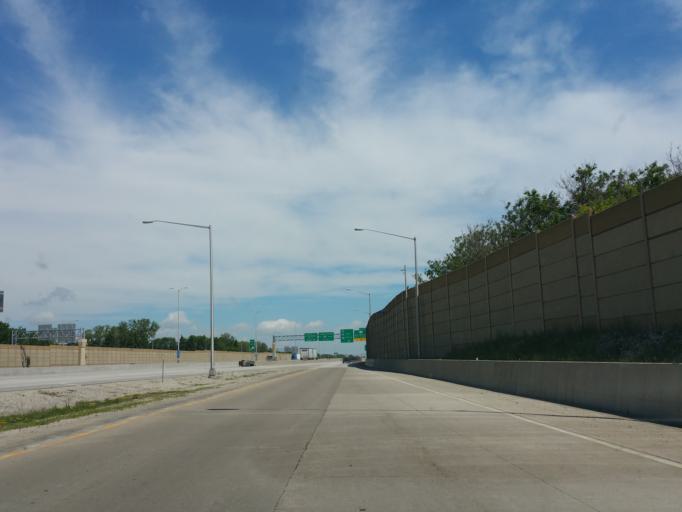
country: US
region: Wisconsin
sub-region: Milwaukee County
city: Greendale
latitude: 42.9327
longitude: -87.9348
